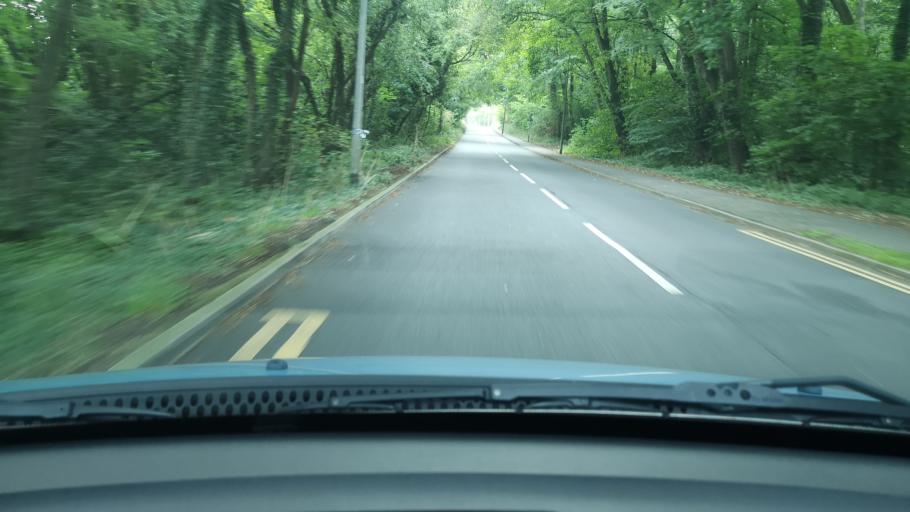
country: GB
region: England
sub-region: North Lincolnshire
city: Scunthorpe
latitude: 53.5845
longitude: -0.6704
